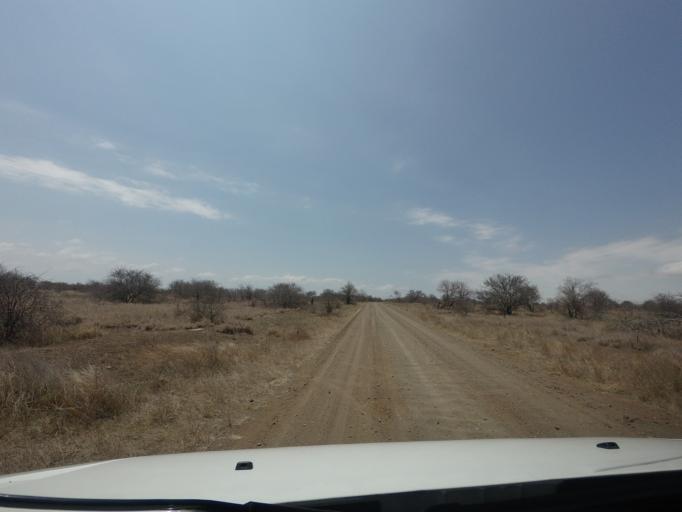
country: ZA
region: Limpopo
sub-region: Mopani District Municipality
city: Phalaborwa
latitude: -24.1018
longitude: 31.6922
